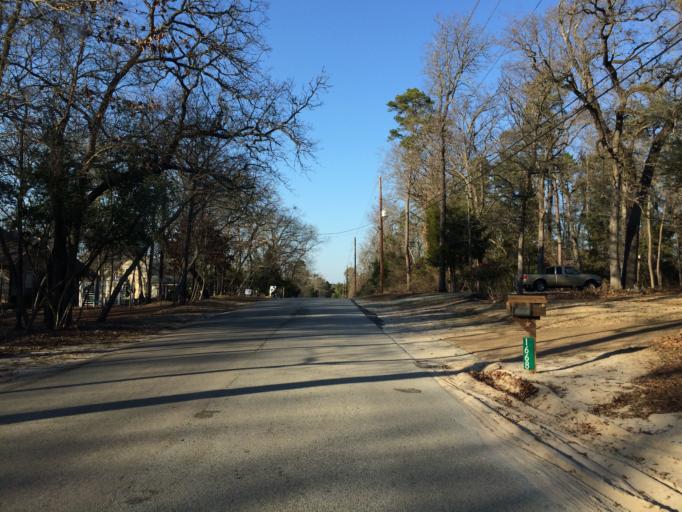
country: US
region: Texas
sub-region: Wood County
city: Hawkins
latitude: 32.7084
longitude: -95.1806
